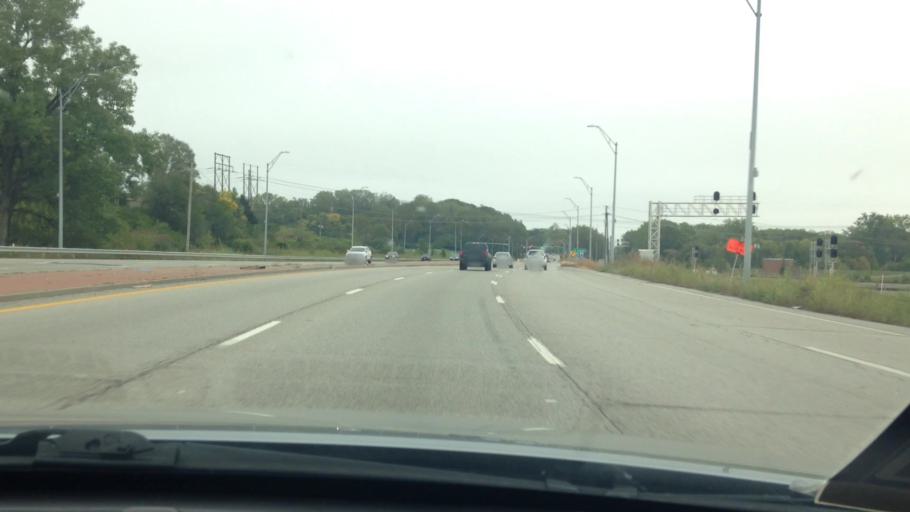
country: US
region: Missouri
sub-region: Clay County
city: North Kansas City
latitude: 39.1464
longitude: -94.5525
